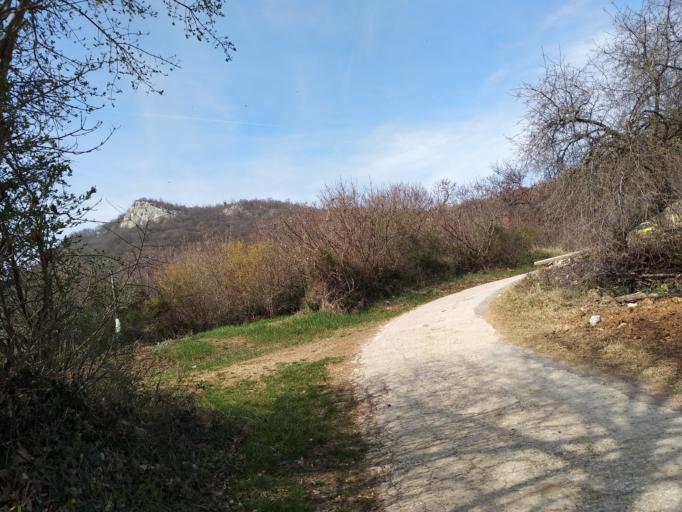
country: IT
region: Veneto
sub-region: Provincia di Vicenza
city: Barbarano Vicentino
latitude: 45.4164
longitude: 11.5379
